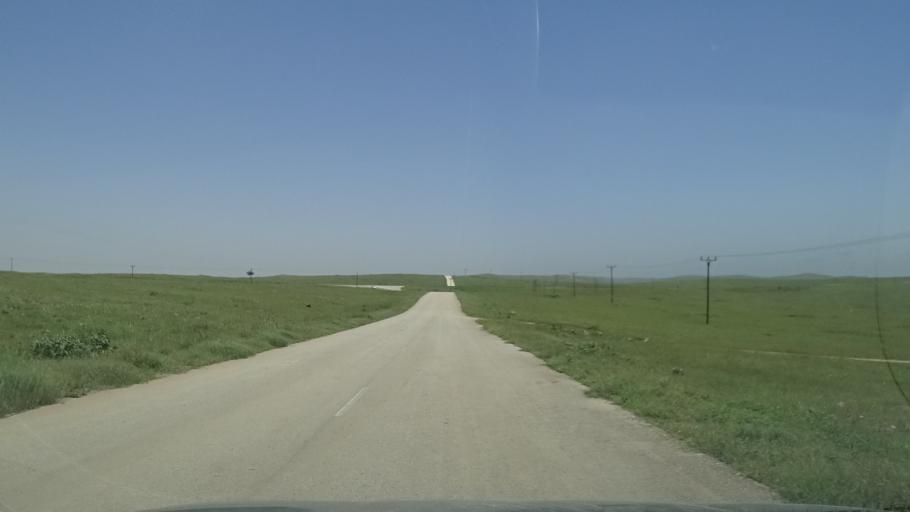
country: OM
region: Zufar
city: Salalah
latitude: 17.2496
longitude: 54.2723
